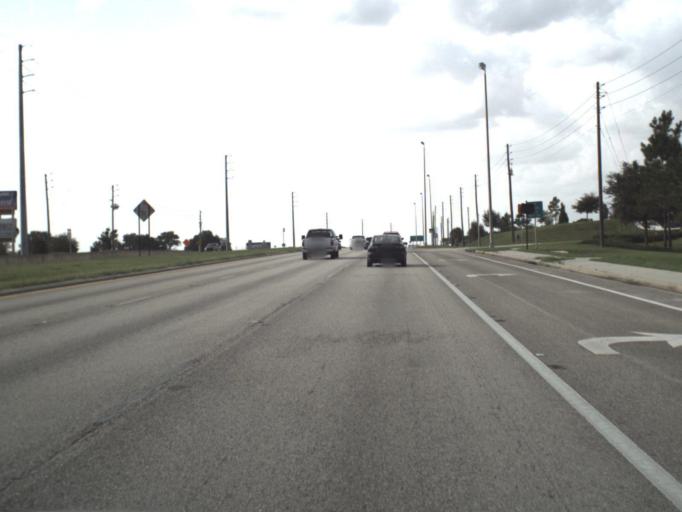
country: US
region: Florida
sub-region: Polk County
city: Loughman
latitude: 28.2383
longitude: -81.6532
